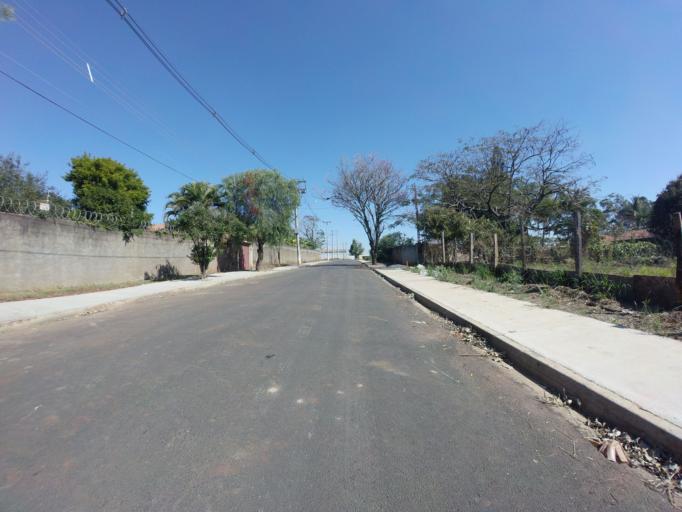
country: BR
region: Sao Paulo
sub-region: Piracicaba
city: Piracicaba
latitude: -22.7594
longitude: -47.5952
